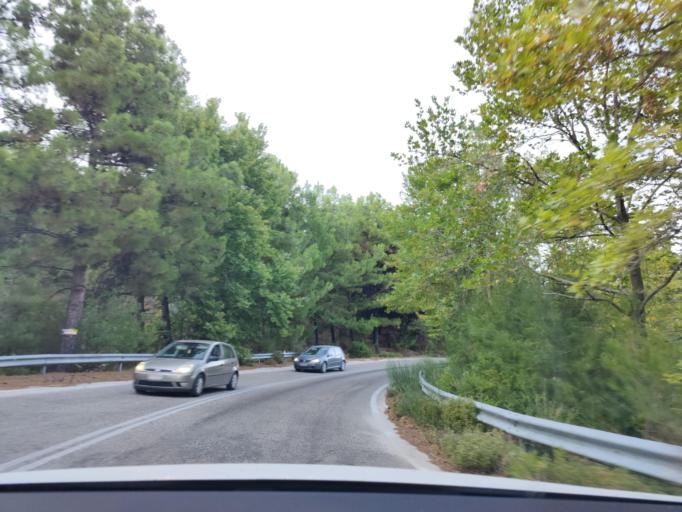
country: GR
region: East Macedonia and Thrace
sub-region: Nomos Kavalas
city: Potamia
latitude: 40.6189
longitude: 24.7584
